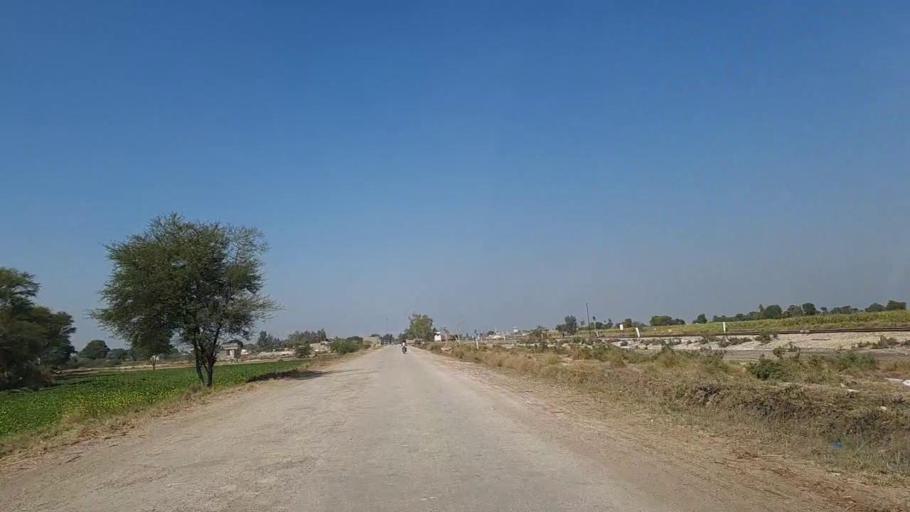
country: PK
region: Sindh
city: Nawabshah
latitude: 26.3450
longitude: 68.3689
